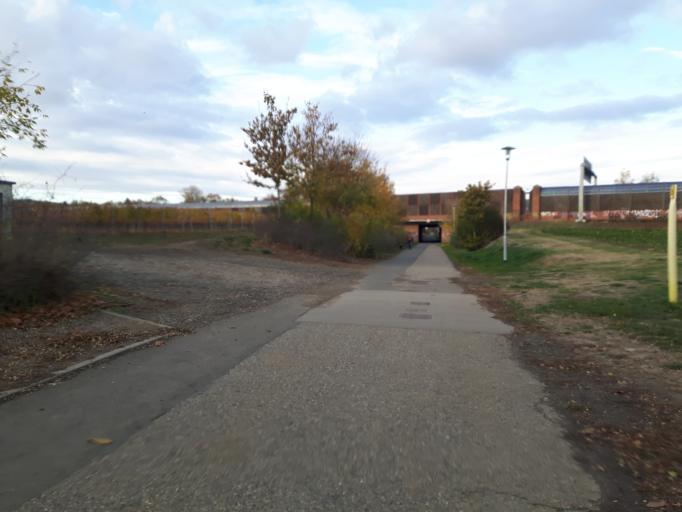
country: DE
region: Rheinland-Pfalz
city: Grunstadt
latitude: 49.5527
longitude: 8.1685
